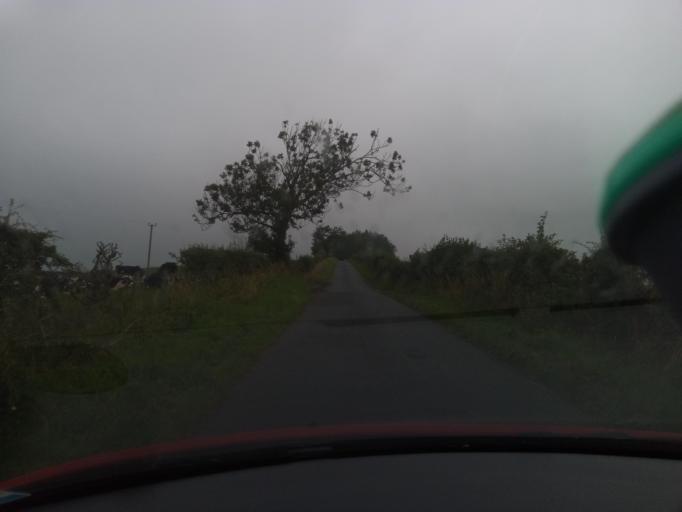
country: GB
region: Scotland
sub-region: The Scottish Borders
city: Earlston
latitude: 55.6485
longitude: -2.7036
